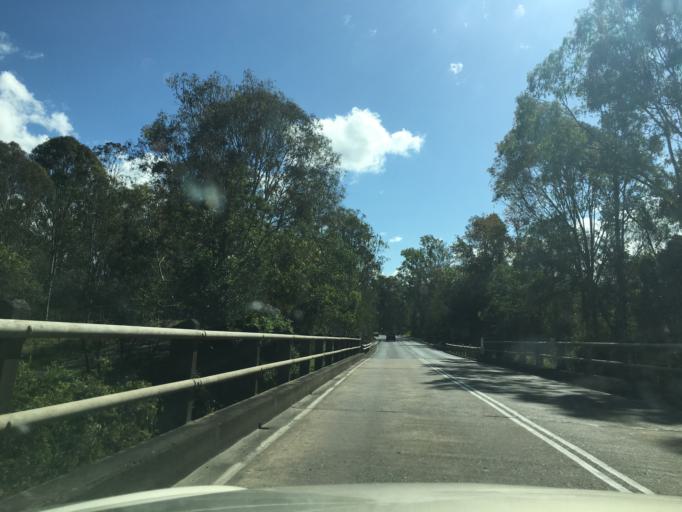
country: AU
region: Queensland
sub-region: Logan
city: Chambers Flat
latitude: -27.7569
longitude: 153.1152
